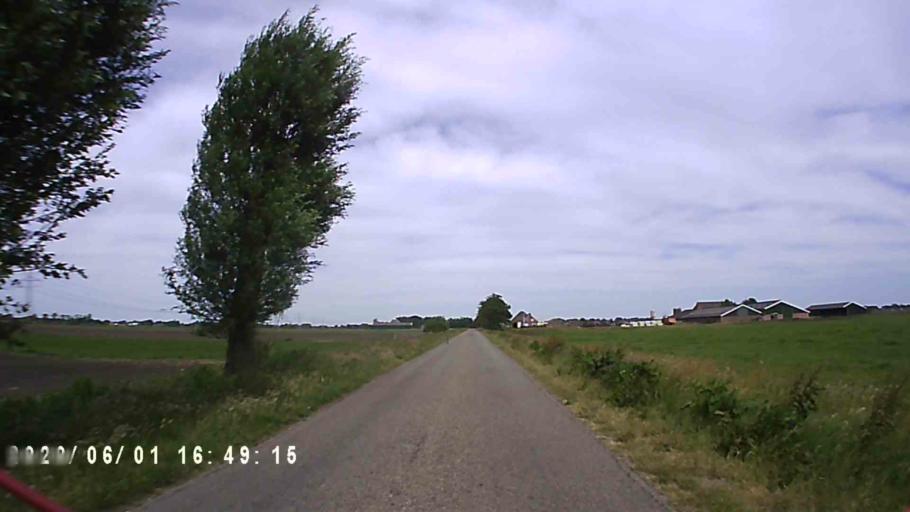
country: NL
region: Friesland
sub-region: Gemeente Tytsjerksteradiel
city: Tytsjerk
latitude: 53.1872
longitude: 5.9053
